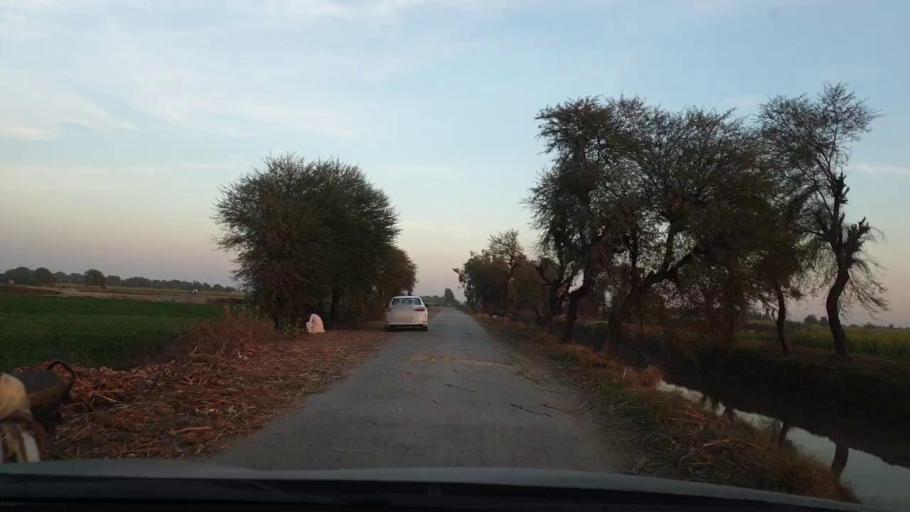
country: PK
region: Sindh
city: Tando Allahyar
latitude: 25.5895
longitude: 68.7136
